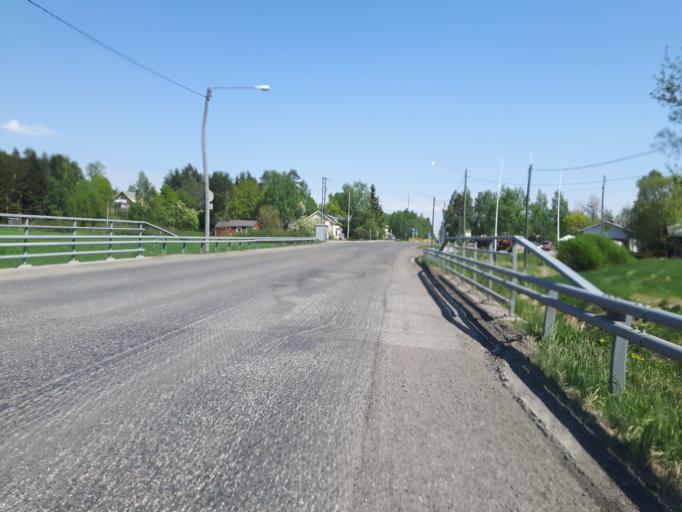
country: FI
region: Uusimaa
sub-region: Helsinki
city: Nickby
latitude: 60.3108
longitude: 25.3866
